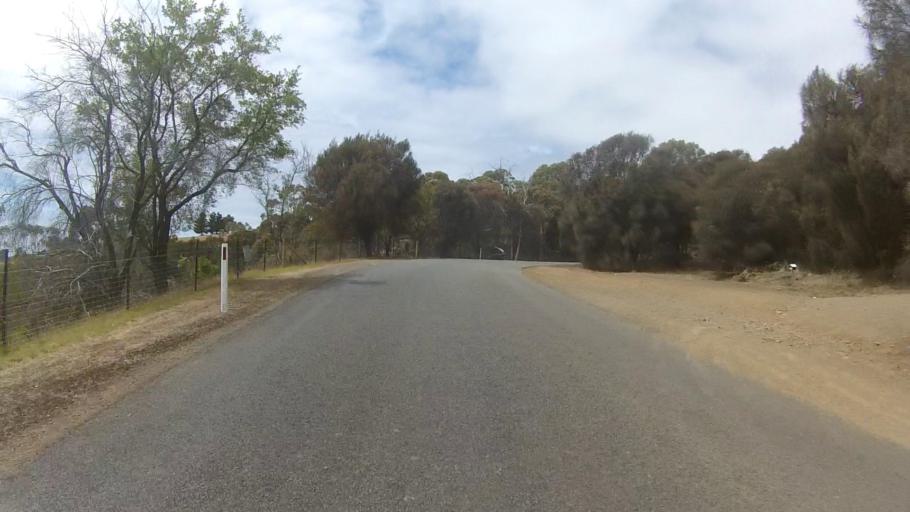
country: AU
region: Tasmania
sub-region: Kingborough
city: Blackmans Bay
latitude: -43.0439
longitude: 147.3342
